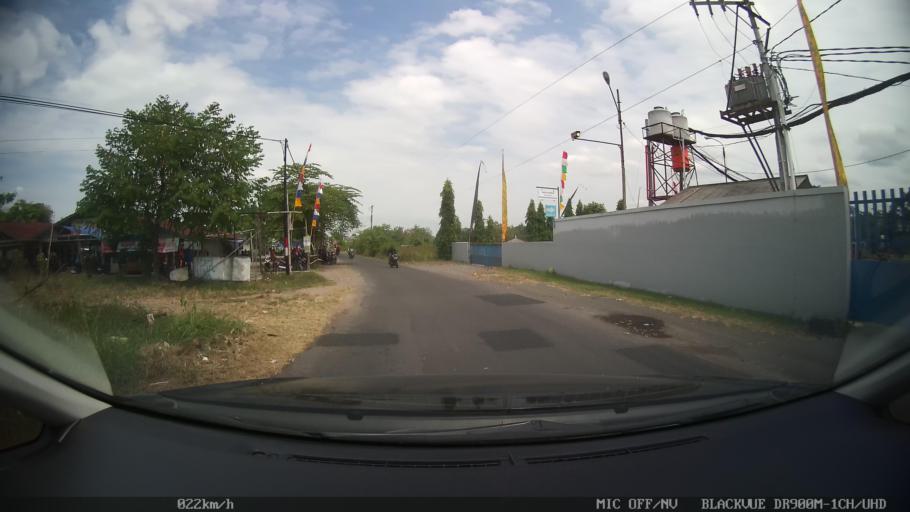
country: ID
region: Central Java
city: Candi Prambanan
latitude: -7.7729
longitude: 110.4792
